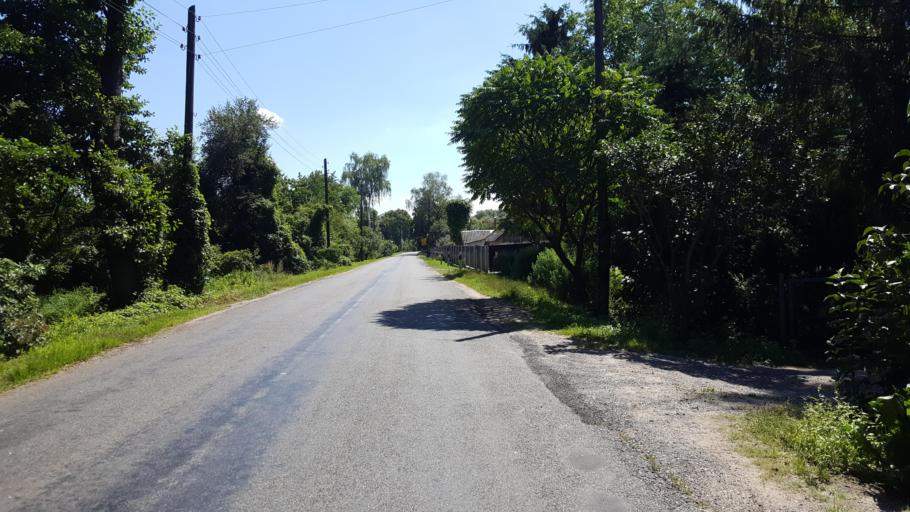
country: BY
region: Brest
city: Charnawchytsy
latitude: 52.3269
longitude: 23.6092
